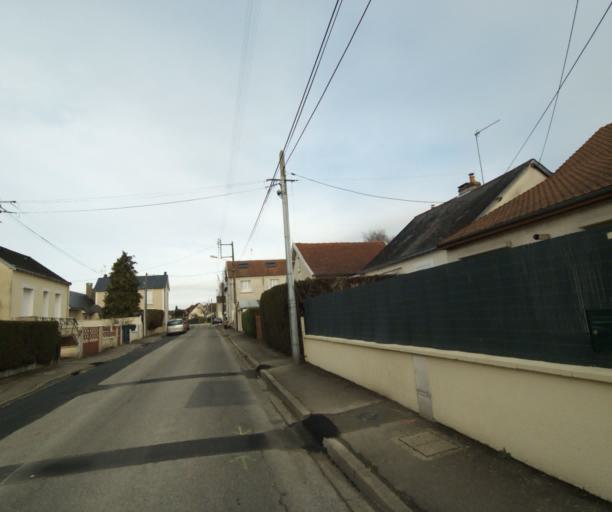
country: FR
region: Pays de la Loire
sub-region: Departement de la Sarthe
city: Le Mans
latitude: 48.0048
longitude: 0.2210
